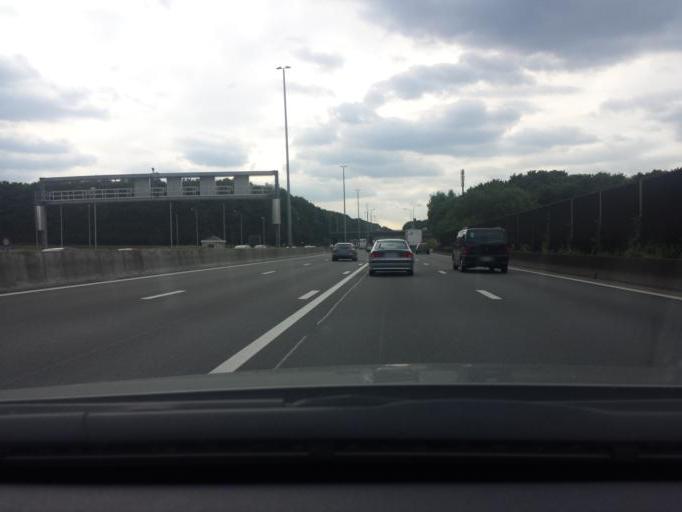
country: BE
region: Flanders
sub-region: Provincie Vlaams-Brabant
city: Bertem
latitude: 50.8604
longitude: 4.6171
